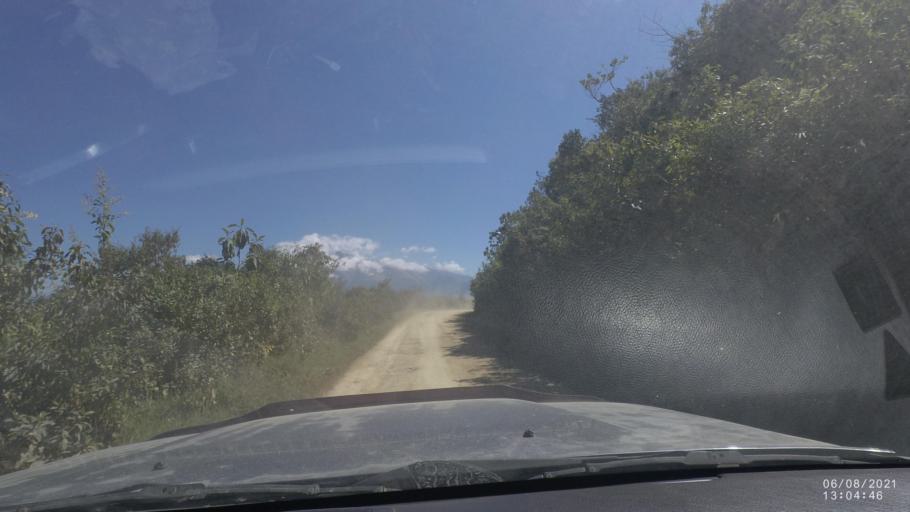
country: BO
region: La Paz
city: Quime
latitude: -16.7354
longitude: -66.6999
